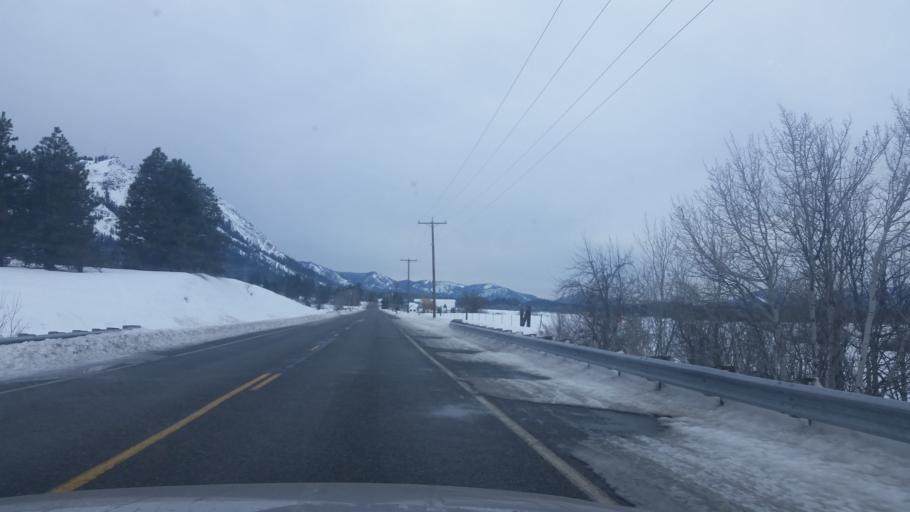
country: US
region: Washington
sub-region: Kittitas County
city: Cle Elum
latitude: 47.1607
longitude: -120.9085
